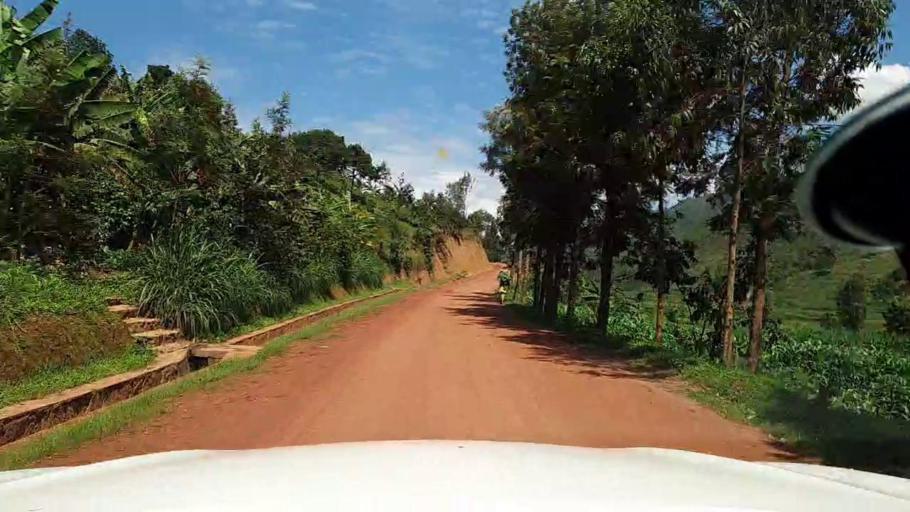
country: RW
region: Kigali
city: Kigali
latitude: -1.7900
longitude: 29.8838
